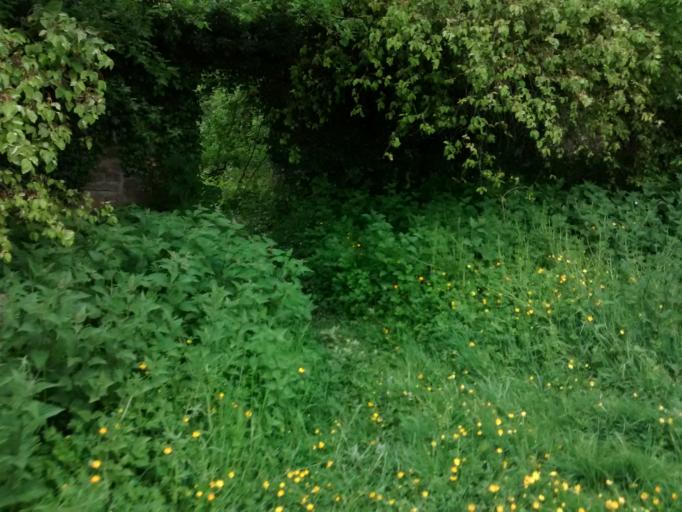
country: GB
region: England
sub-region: County Durham
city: Durham
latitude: 54.7718
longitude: -1.5555
